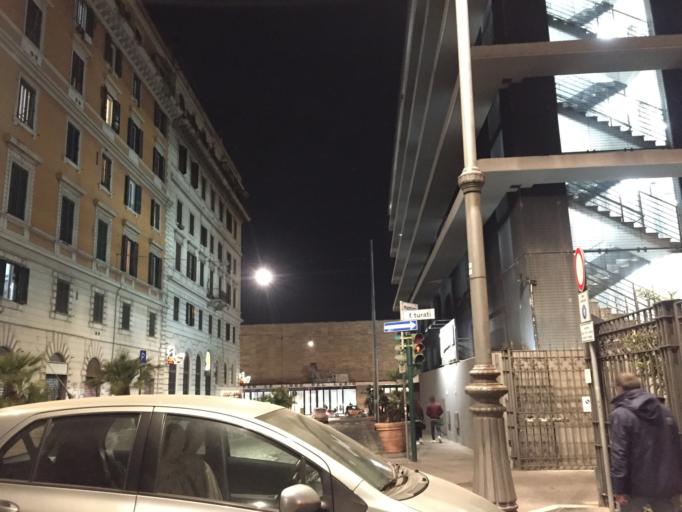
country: IT
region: Latium
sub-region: Citta metropolitana di Roma Capitale
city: Rome
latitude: 41.8966
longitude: 12.5054
